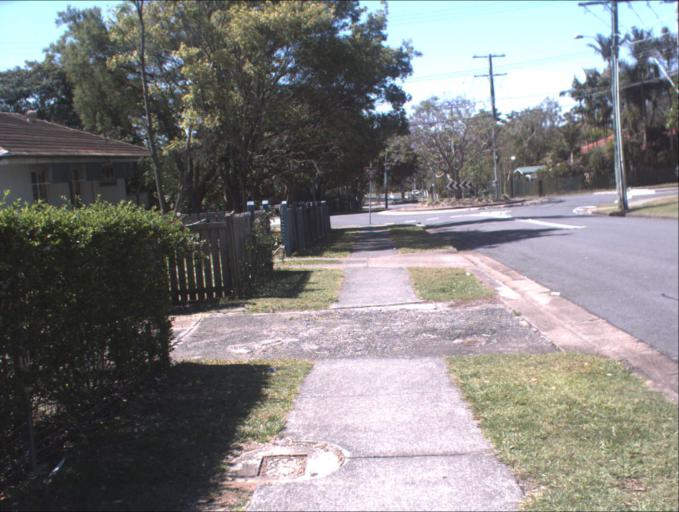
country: AU
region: Queensland
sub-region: Logan
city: Logan City
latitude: -27.6377
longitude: 153.1127
